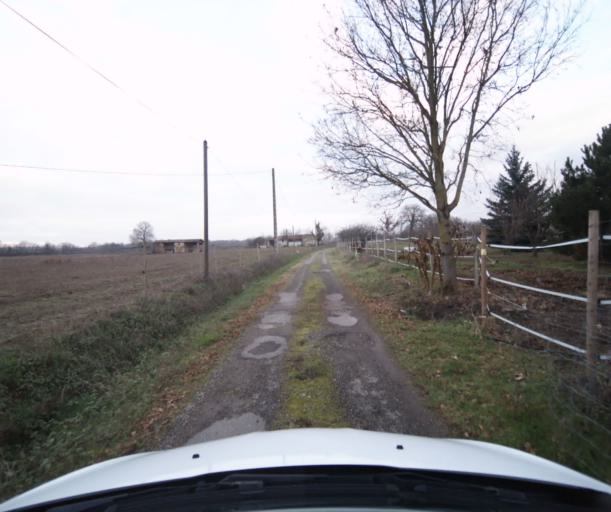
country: FR
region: Midi-Pyrenees
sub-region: Departement du Tarn-et-Garonne
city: Moissac
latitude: 44.0700
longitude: 1.1034
